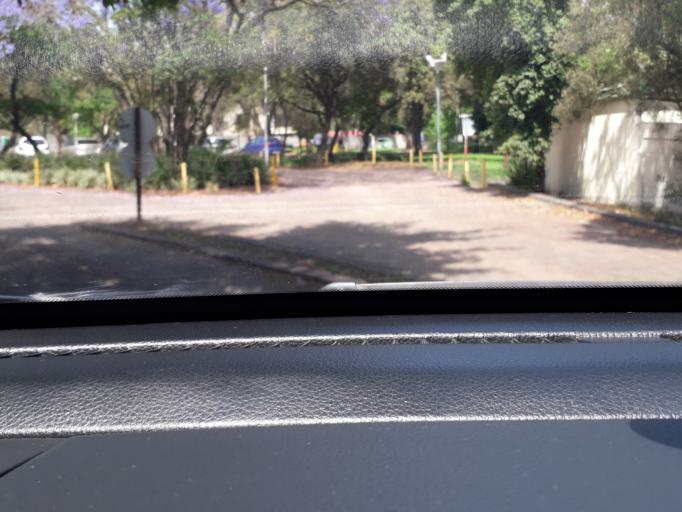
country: ZA
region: Gauteng
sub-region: City of Johannesburg Metropolitan Municipality
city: Modderfontein
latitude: -26.0788
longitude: 28.0738
